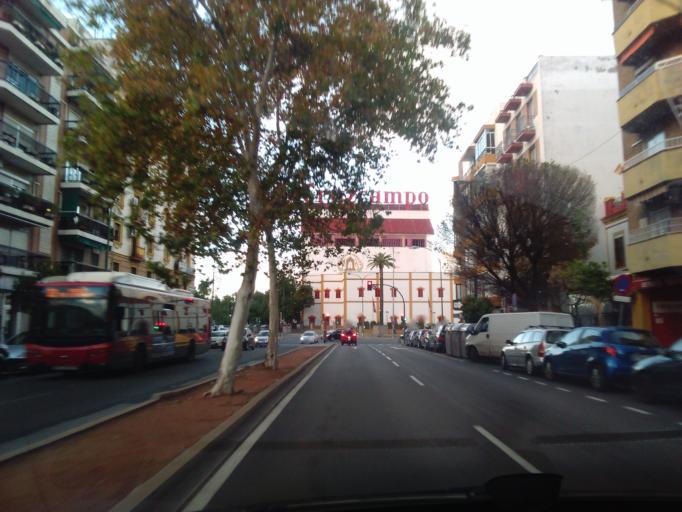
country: ES
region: Andalusia
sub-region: Provincia de Sevilla
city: Sevilla
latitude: 37.3869
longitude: -5.9652
